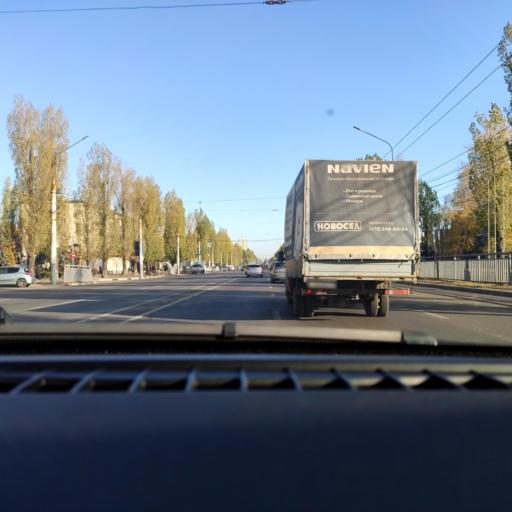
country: RU
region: Voronezj
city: Voronezh
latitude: 51.6901
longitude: 39.2670
